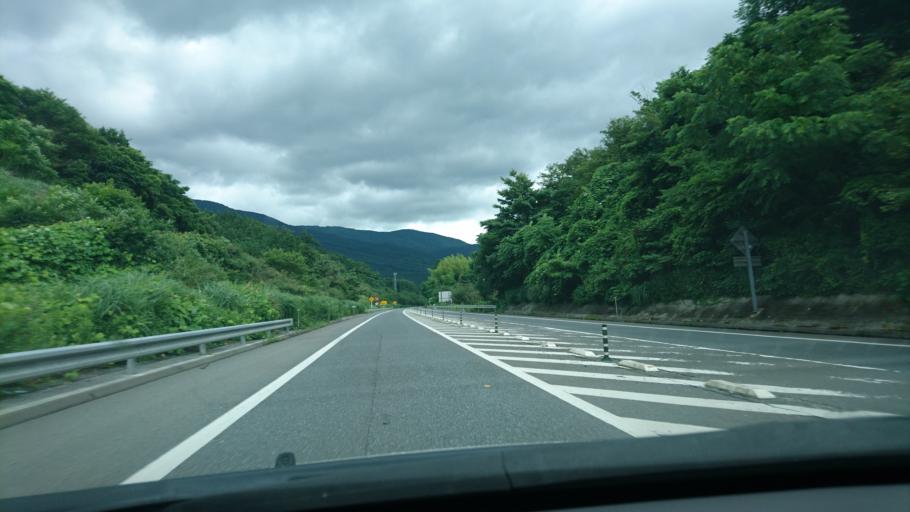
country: JP
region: Iwate
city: Ofunato
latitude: 39.1159
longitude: 141.7133
